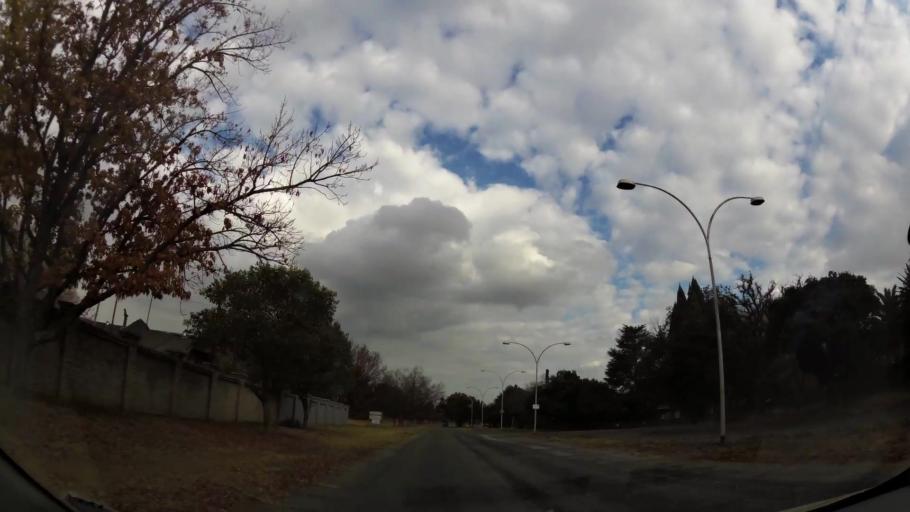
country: ZA
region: Orange Free State
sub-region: Fezile Dabi District Municipality
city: Sasolburg
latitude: -26.7908
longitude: 27.8225
